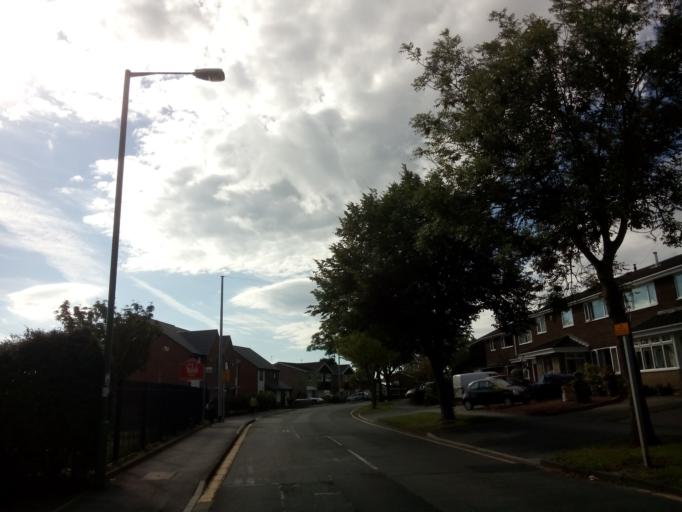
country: GB
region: England
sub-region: County Durham
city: Durham
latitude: 54.8021
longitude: -1.5642
